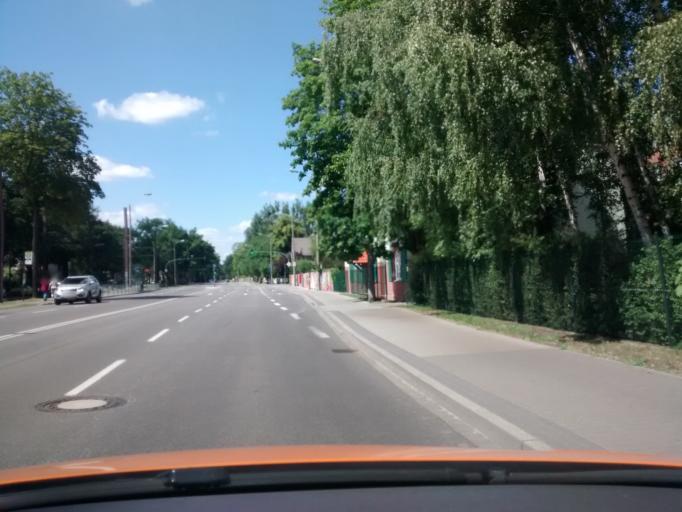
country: DE
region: Brandenburg
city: Potsdam
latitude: 52.3770
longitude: 13.0840
